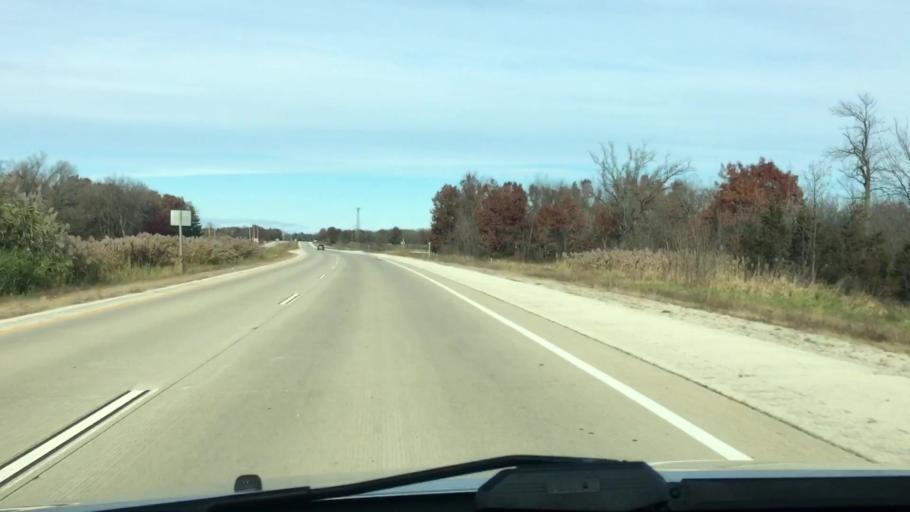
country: US
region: Wisconsin
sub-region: Brown County
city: Bellevue
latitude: 44.5859
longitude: -87.8672
